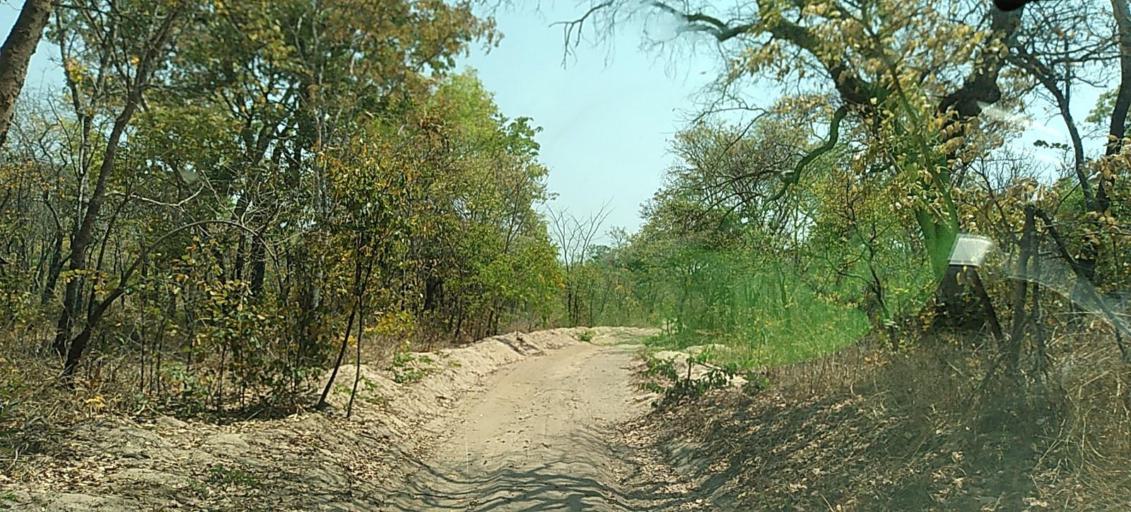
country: ZM
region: North-Western
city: Kalengwa
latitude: -13.1119
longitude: 24.6905
